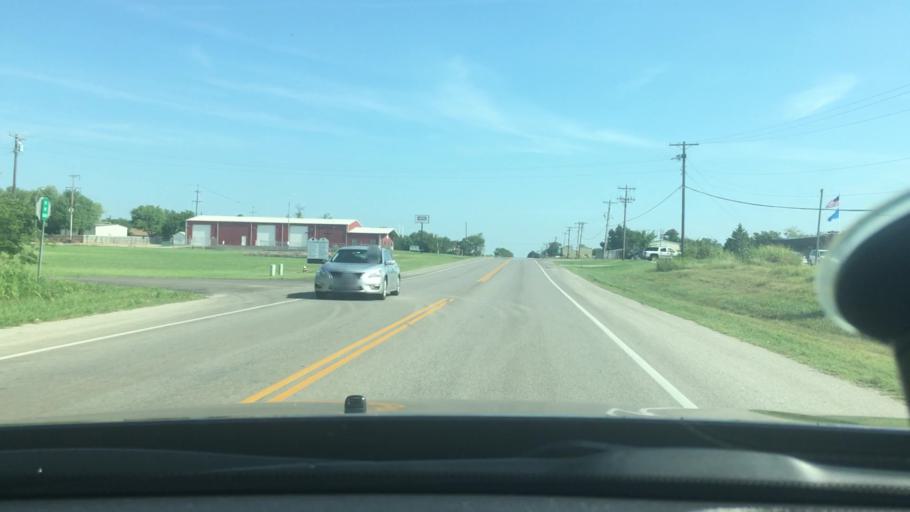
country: US
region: Oklahoma
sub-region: Garvin County
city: Pauls Valley
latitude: 34.7037
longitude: -97.2128
